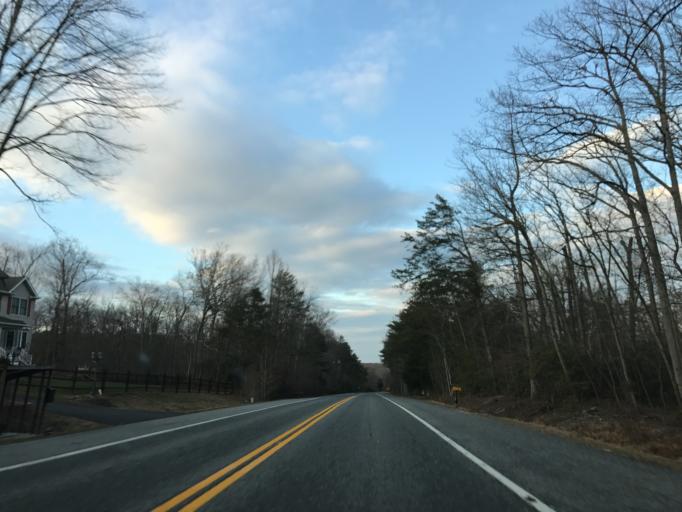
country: US
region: Maryland
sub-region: Cecil County
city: Charlestown
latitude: 39.5268
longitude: -75.9537
